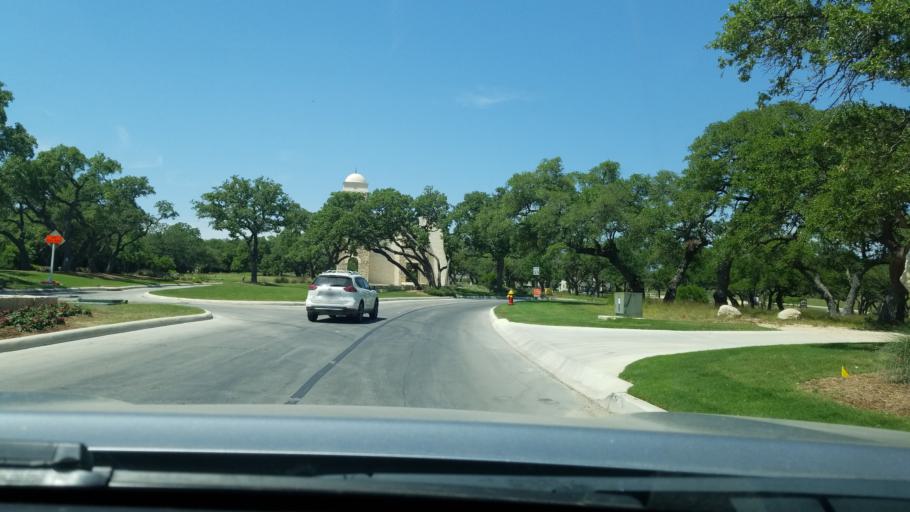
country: US
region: Texas
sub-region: Kendall County
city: Boerne
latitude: 29.7874
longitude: -98.6931
